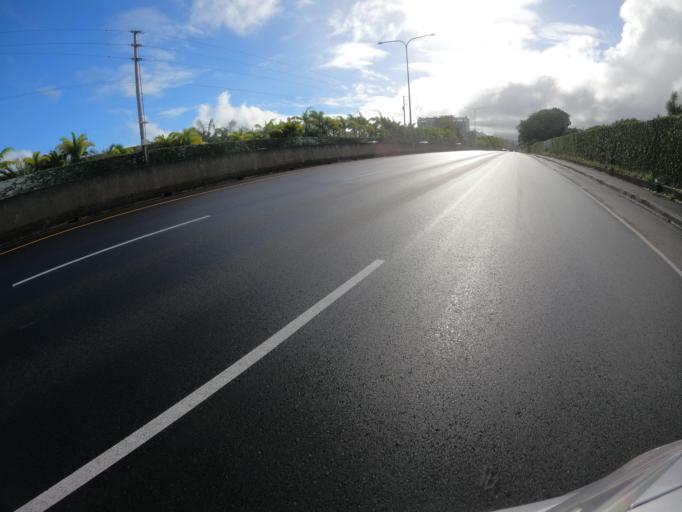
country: US
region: Hawaii
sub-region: Honolulu County
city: He'eia
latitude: 21.4163
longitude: -157.8132
